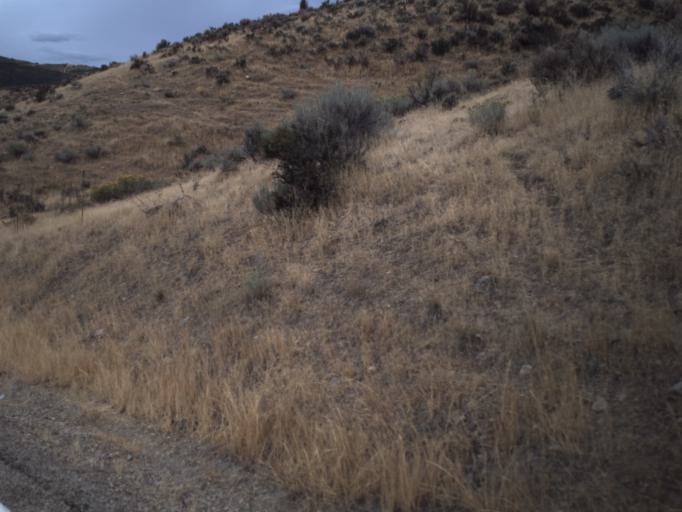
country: US
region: Utah
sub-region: Morgan County
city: Morgan
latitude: 40.9237
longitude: -111.5753
